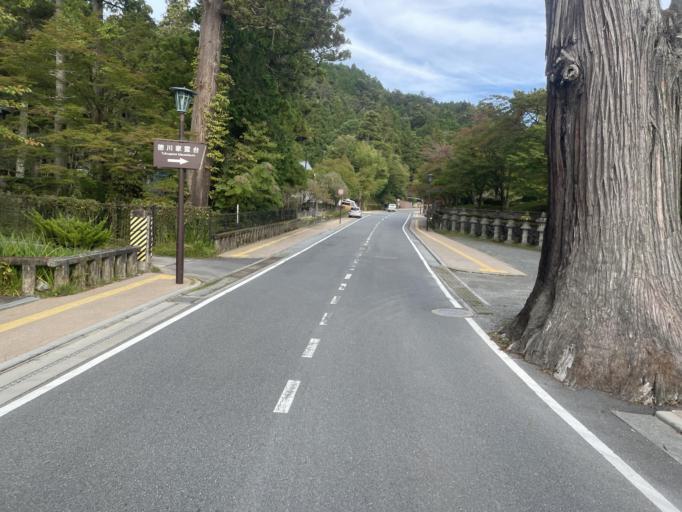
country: JP
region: Wakayama
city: Koya
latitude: 34.2168
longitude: 135.5823
